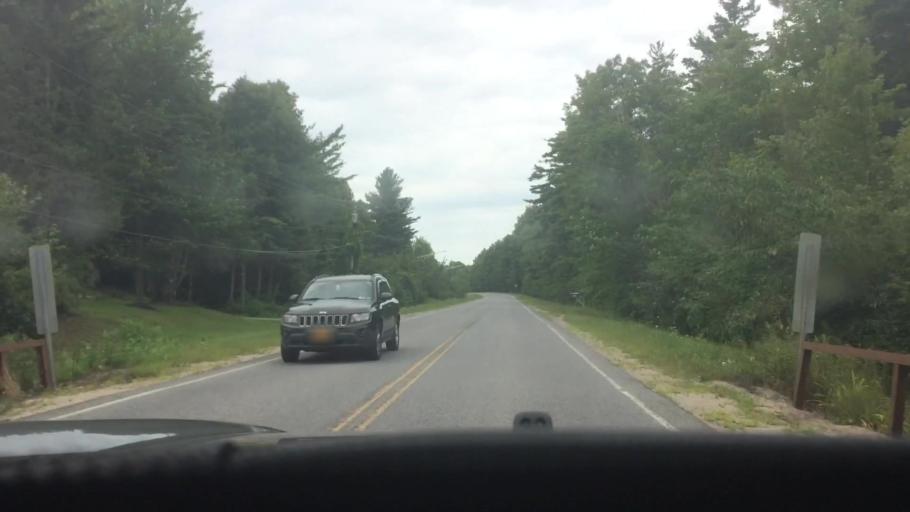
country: US
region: New York
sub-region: St. Lawrence County
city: Hannawa Falls
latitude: 44.5481
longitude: -74.9305
